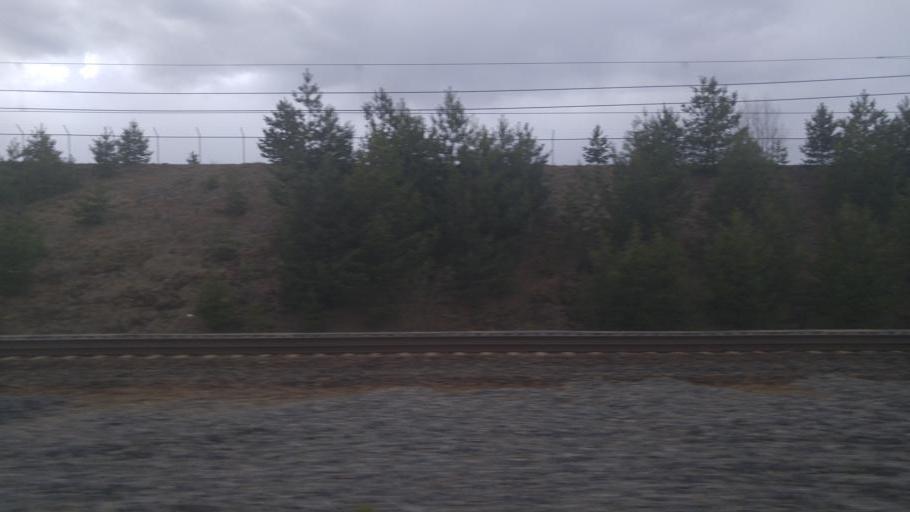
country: NO
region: Akershus
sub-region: Nannestad
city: Teigebyen
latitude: 60.2019
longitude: 11.1019
